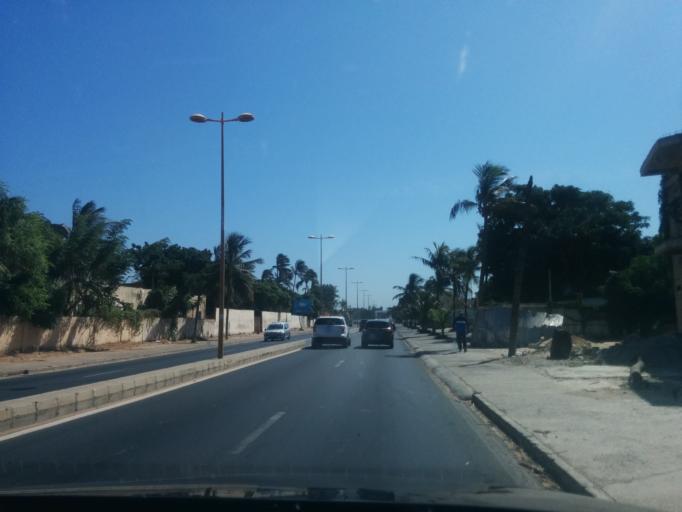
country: SN
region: Dakar
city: Mermoz Boabab
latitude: 14.7038
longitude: -17.4801
